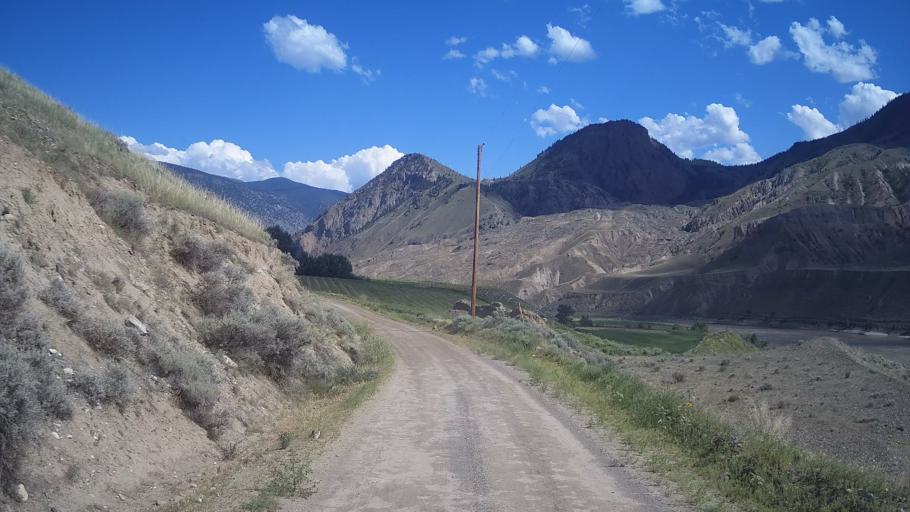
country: CA
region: British Columbia
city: Lillooet
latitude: 51.1811
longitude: -122.1205
